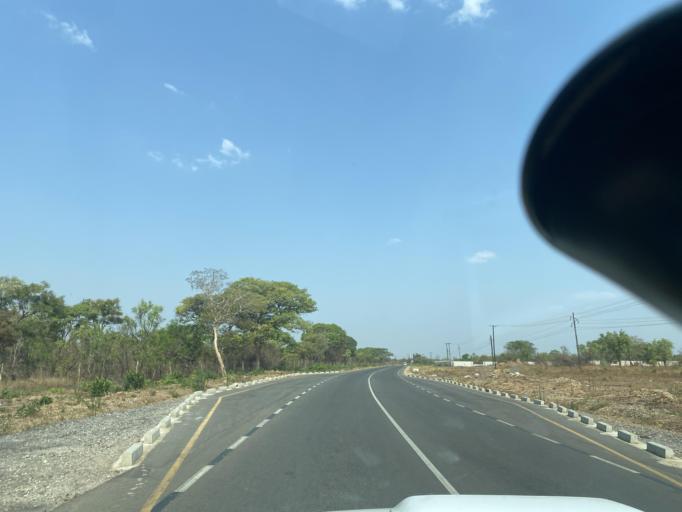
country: ZM
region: Lusaka
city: Lusaka
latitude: -15.3468
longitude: 28.0959
